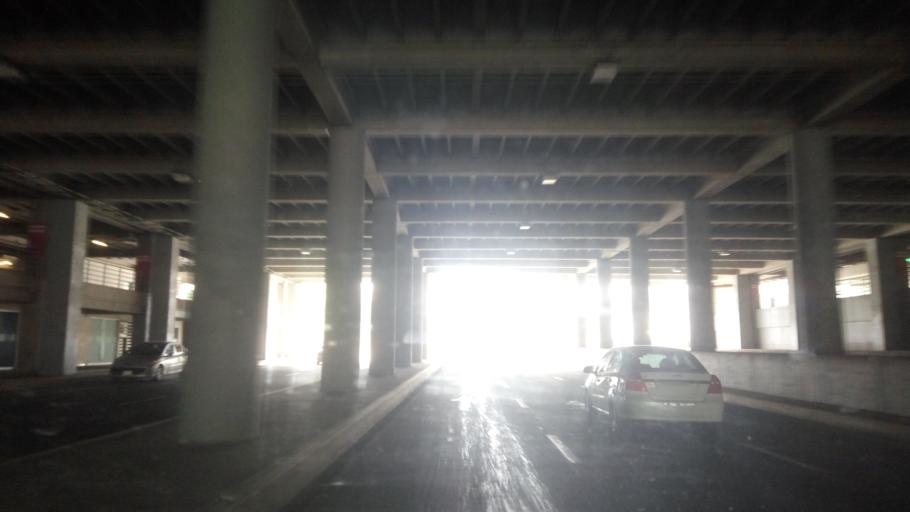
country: MX
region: Tabasco
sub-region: Nacajuca
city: Bosque de Saloya
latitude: 18.0009
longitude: -92.9463
